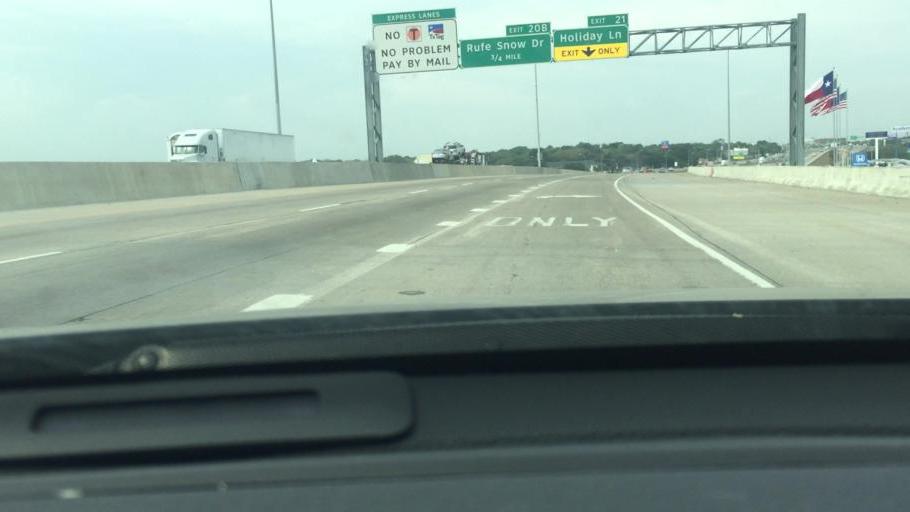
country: US
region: Texas
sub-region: Tarrant County
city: North Richland Hills
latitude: 32.8334
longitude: -97.2163
